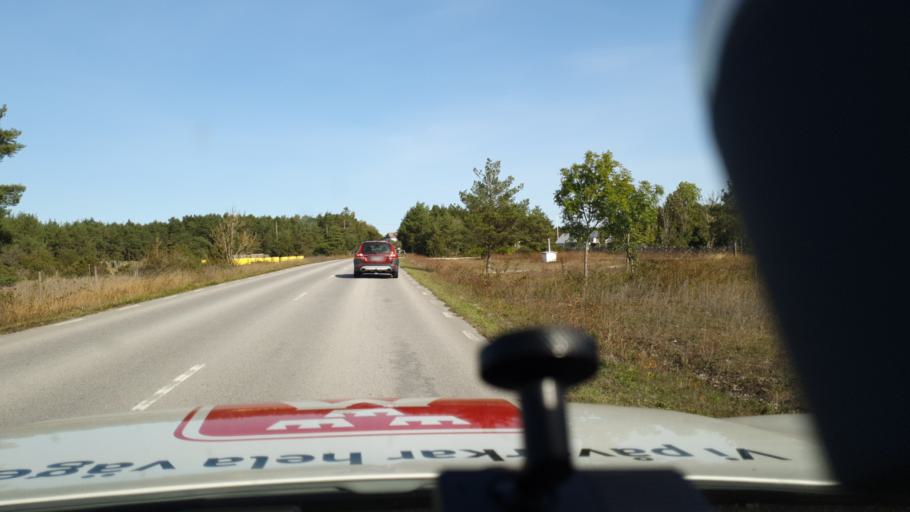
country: SE
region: Gotland
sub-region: Gotland
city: Slite
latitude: 57.8902
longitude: 19.0905
